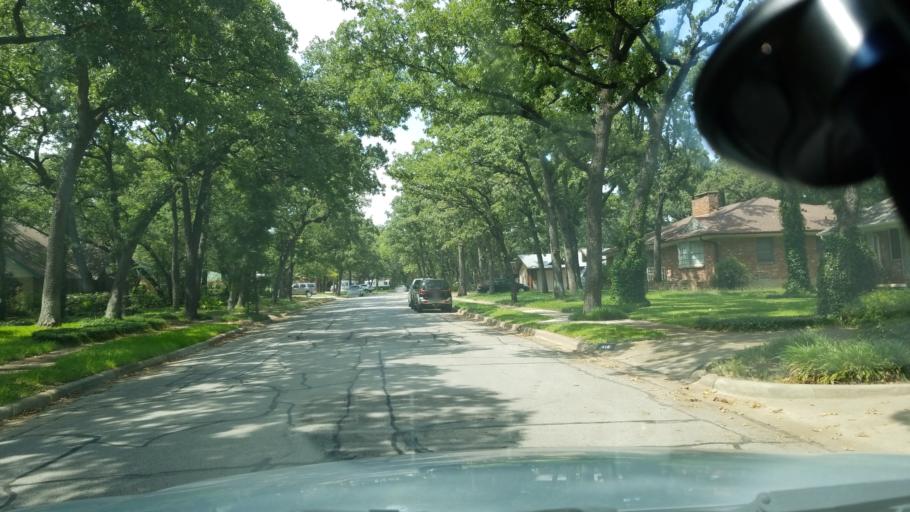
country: US
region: Texas
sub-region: Dallas County
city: Irving
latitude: 32.8197
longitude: -96.9828
